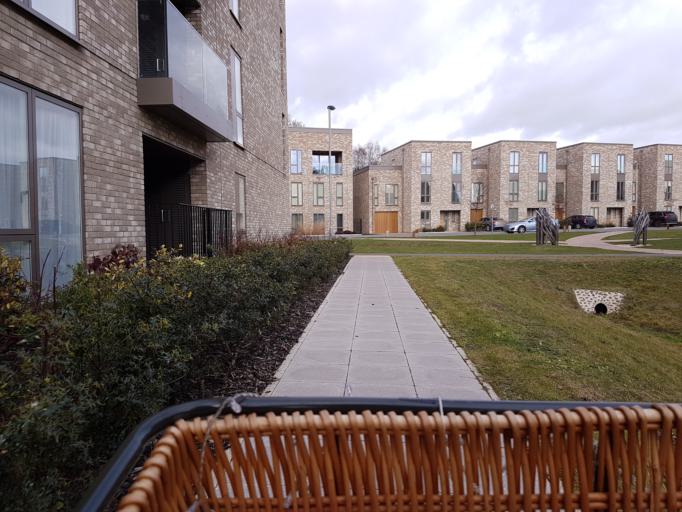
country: GB
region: England
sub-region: Cambridgeshire
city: Cambridge
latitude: 52.1719
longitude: 0.1428
